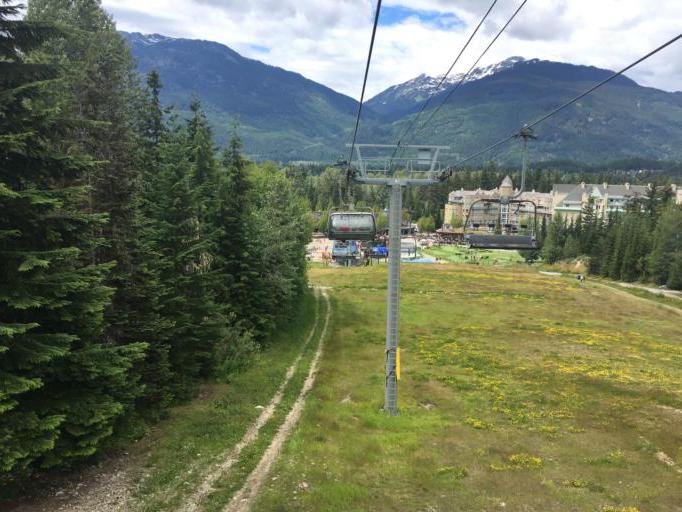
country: CA
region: British Columbia
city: Whistler
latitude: 50.1145
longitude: -122.9449
